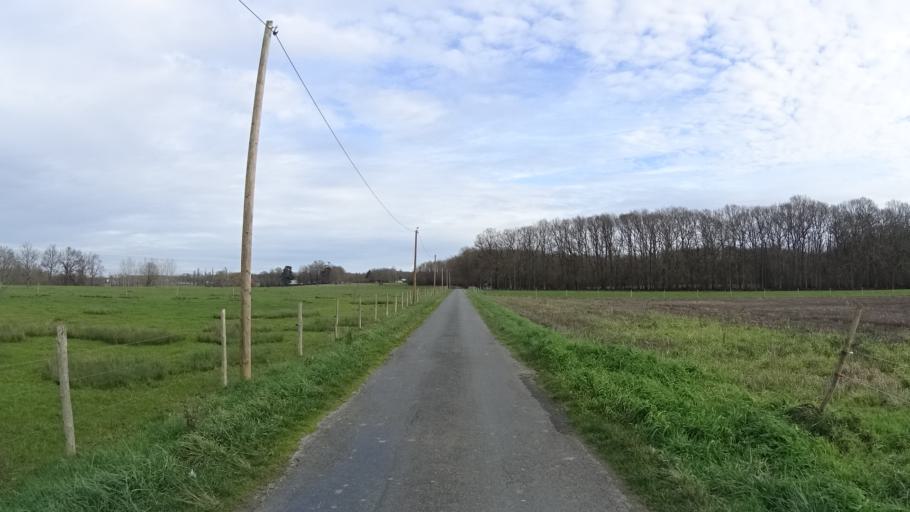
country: FR
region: Aquitaine
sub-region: Departement de la Dordogne
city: Saint-Aulaye
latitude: 45.2252
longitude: 0.1527
